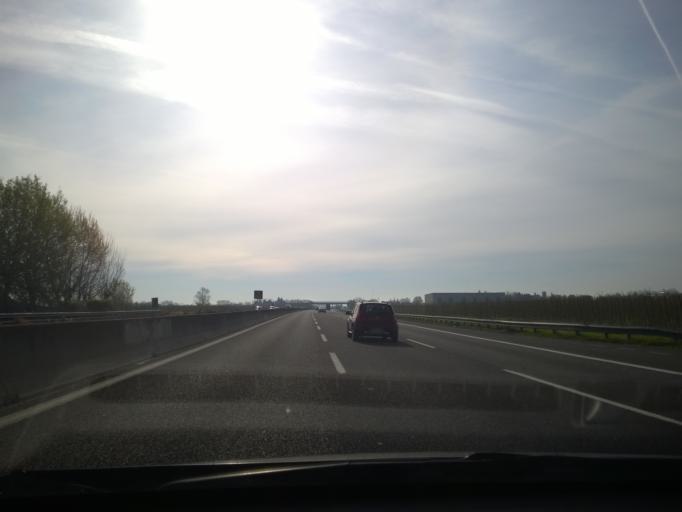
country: IT
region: Emilia-Romagna
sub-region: Provincia di Bologna
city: Bubano
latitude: 44.3700
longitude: 11.7719
